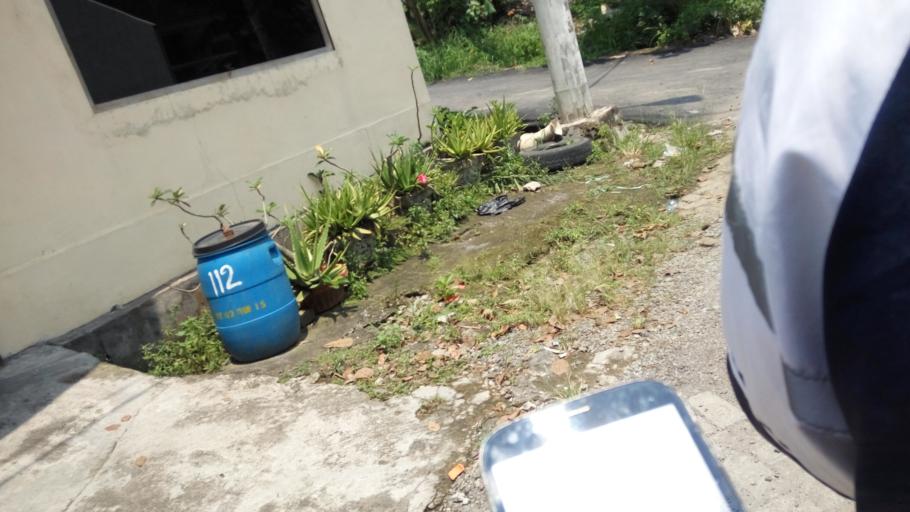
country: ID
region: Central Java
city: Mranggen
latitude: -7.0452
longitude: 110.4734
